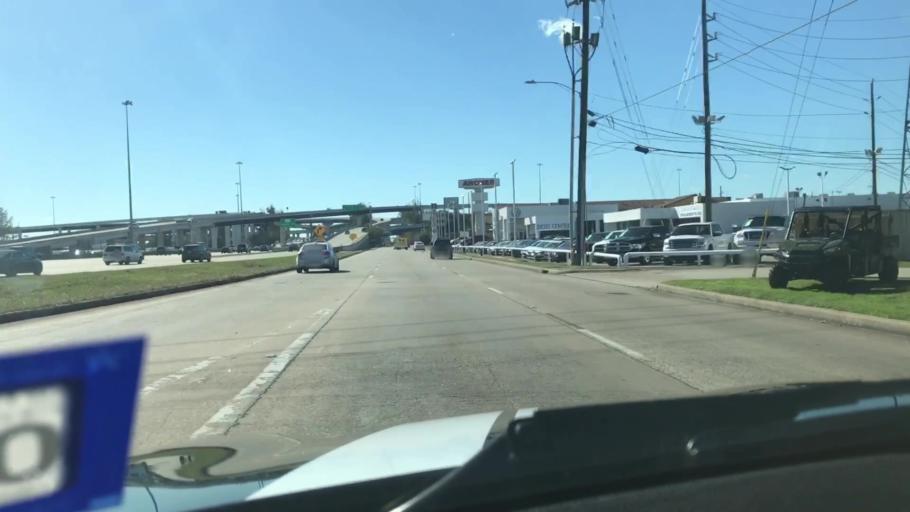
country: US
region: Texas
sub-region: Fort Bend County
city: Meadows Place
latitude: 29.6663
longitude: -95.5530
